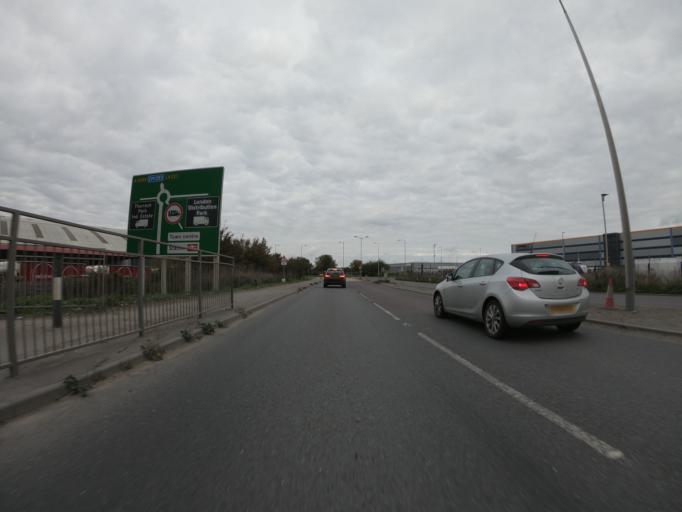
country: GB
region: England
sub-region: Borough of Thurrock
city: Tilbury
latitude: 51.4675
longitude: 0.3477
